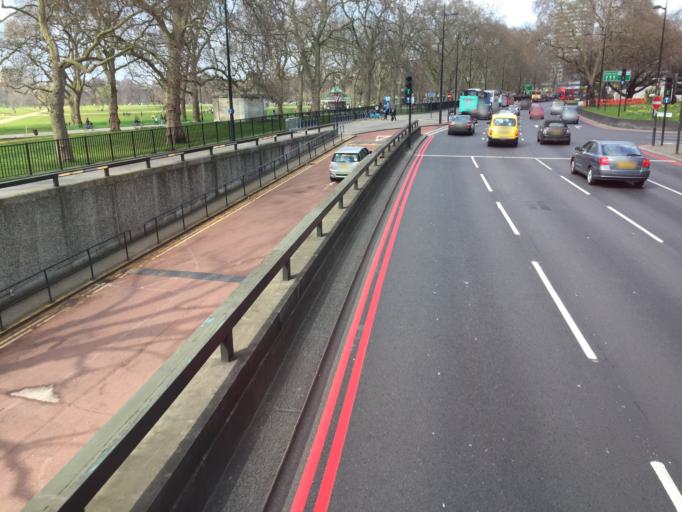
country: GB
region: England
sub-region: Greater London
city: Chelsea
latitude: 51.5096
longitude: -0.1565
